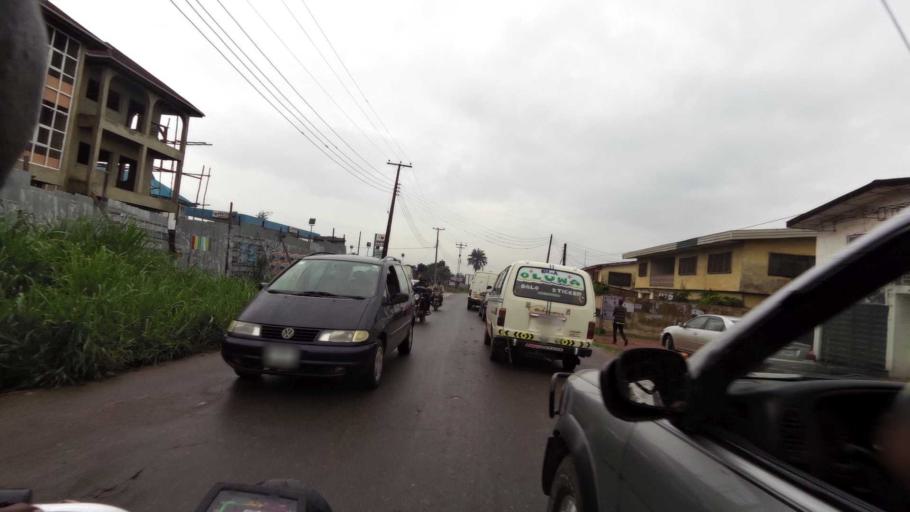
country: NG
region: Oyo
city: Ibadan
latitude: 7.4067
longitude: 3.9278
